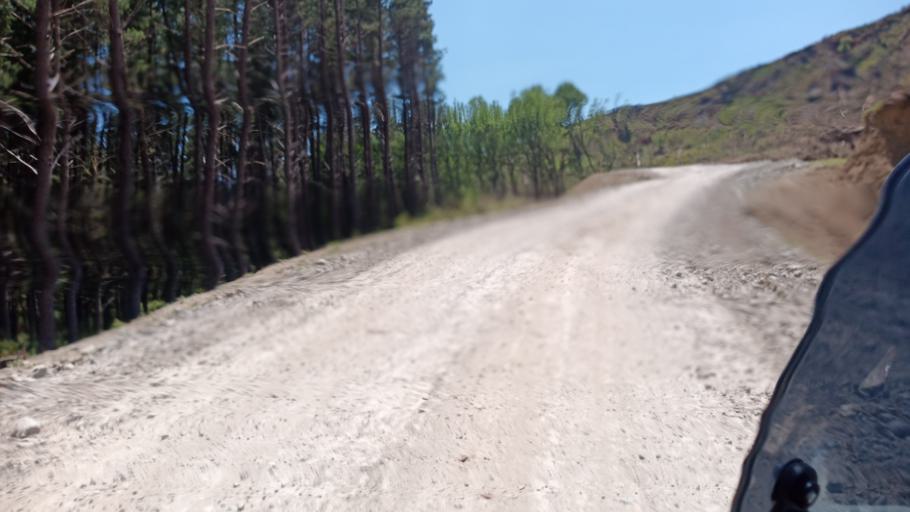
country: NZ
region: Gisborne
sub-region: Gisborne District
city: Gisborne
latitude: -38.2818
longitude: 177.9983
